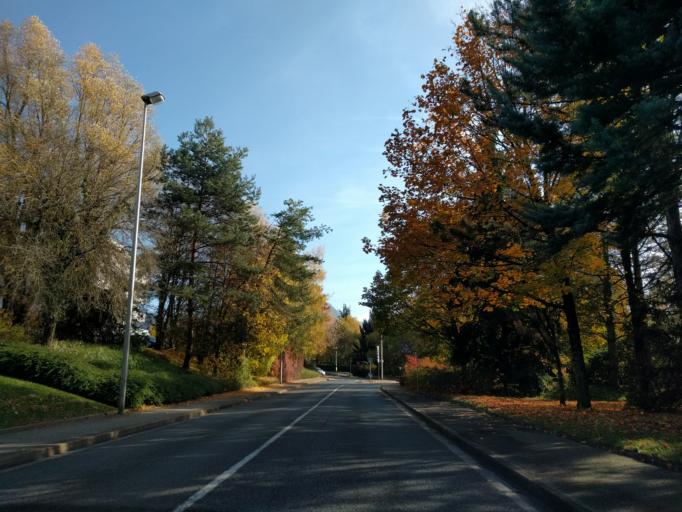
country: FR
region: Rhone-Alpes
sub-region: Departement de la Haute-Savoie
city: Annecy-le-Vieux
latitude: 45.9221
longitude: 6.1327
